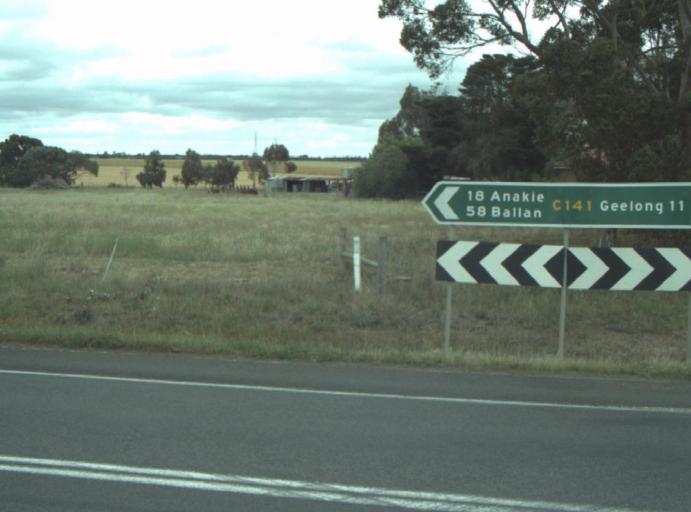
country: AU
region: Victoria
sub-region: Greater Geelong
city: Bell Post Hill
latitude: -38.0664
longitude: 144.2921
